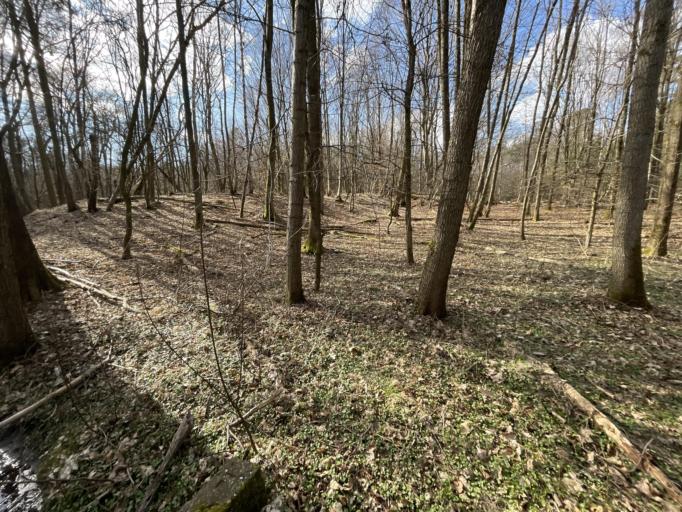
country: DE
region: Hesse
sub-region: Regierungsbezirk Darmstadt
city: Offenbach
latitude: 50.0701
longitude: 8.7649
